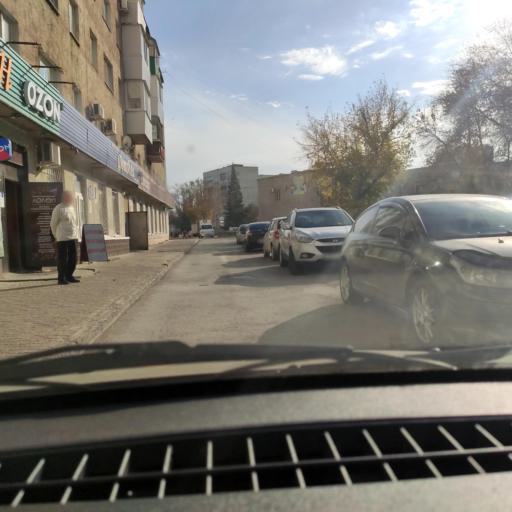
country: RU
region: Bashkortostan
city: Avdon
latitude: 54.7007
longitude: 55.8274
